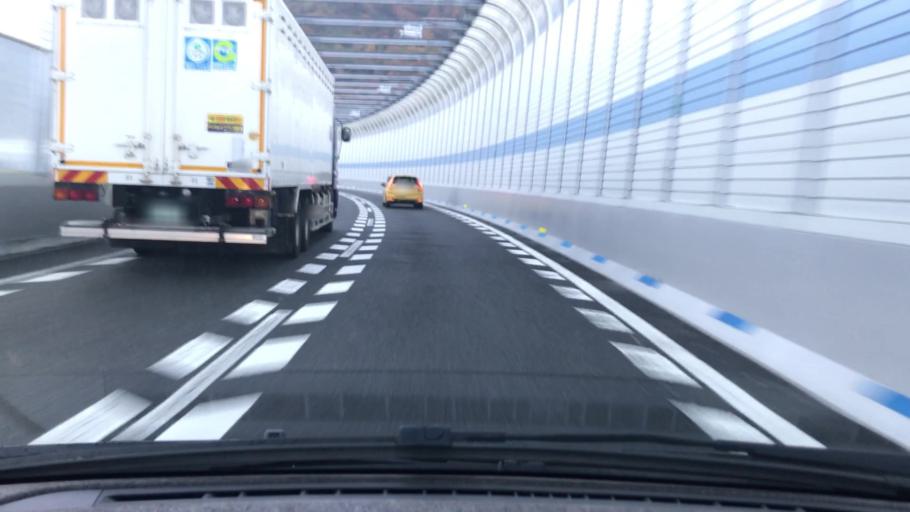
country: JP
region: Hyogo
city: Sandacho
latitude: 34.8212
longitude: 135.2607
